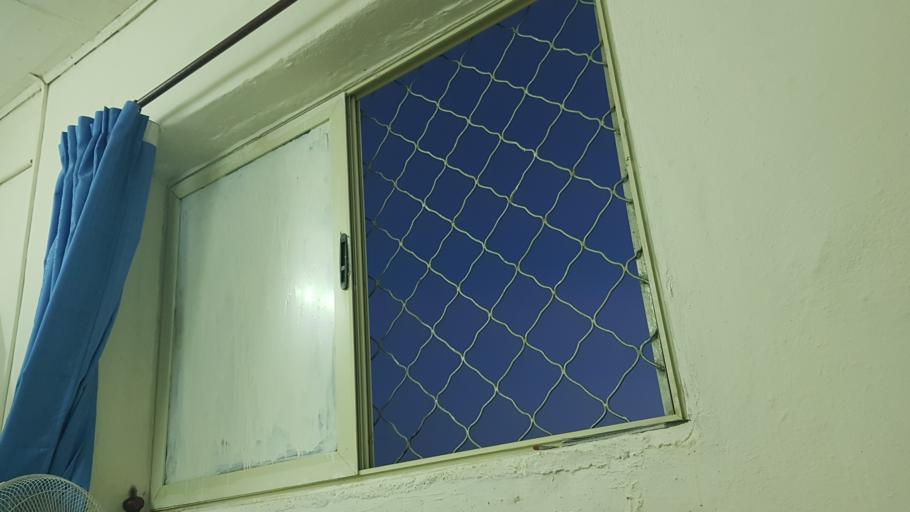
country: ET
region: Oromiya
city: Shambu
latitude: 9.9103
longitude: 36.7474
